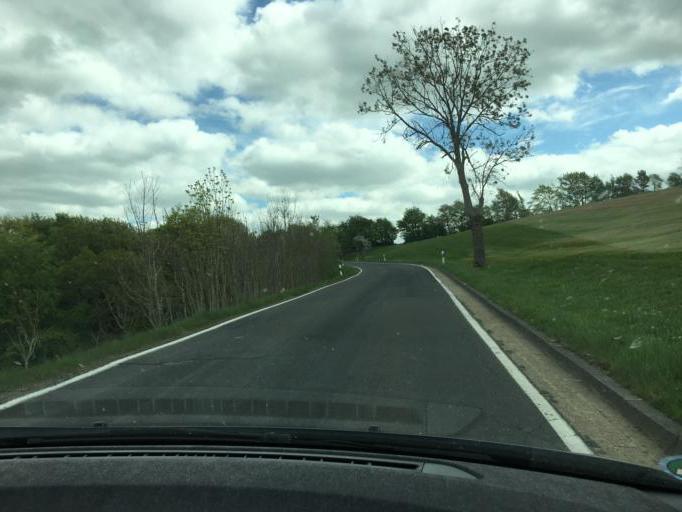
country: DE
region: Rheinland-Pfalz
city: Lind
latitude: 50.4930
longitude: 6.9266
